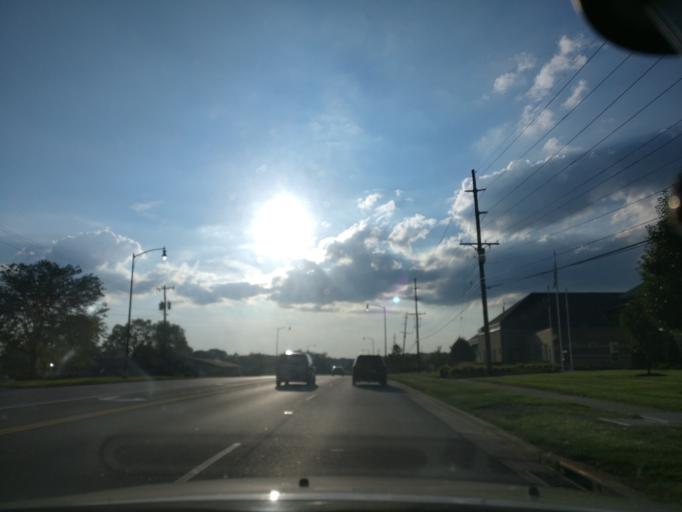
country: US
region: Ohio
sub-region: Warren County
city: Springboro
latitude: 39.5593
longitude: -84.2418
